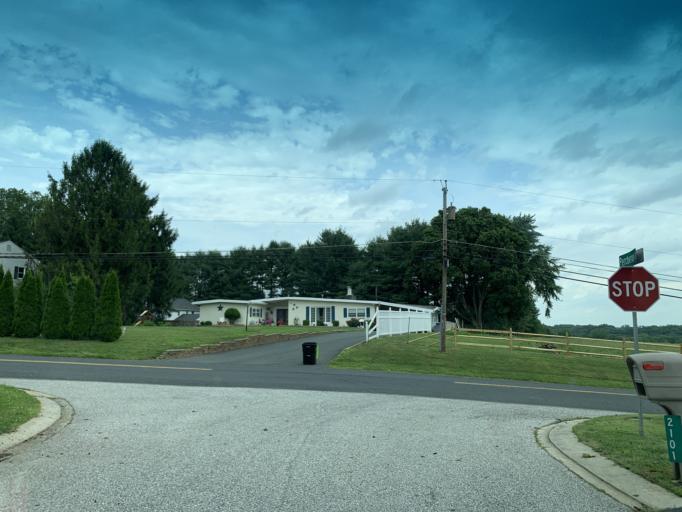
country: US
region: Maryland
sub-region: Harford County
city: Fallston
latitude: 39.5364
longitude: -76.4330
